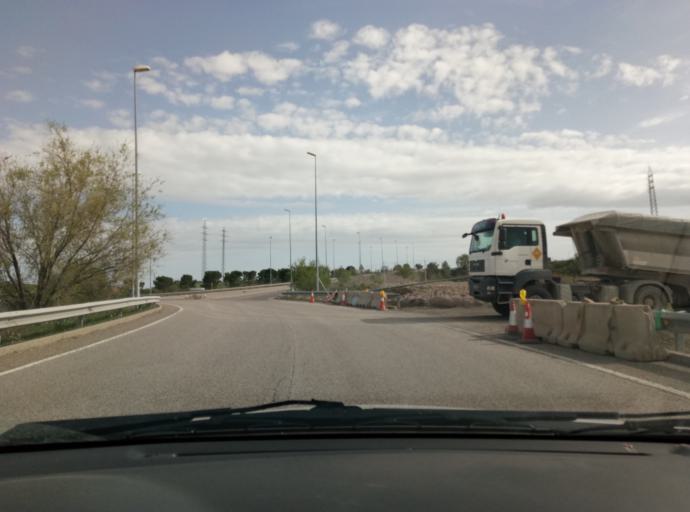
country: ES
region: Catalonia
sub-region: Provincia de Lleida
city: Cervera
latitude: 41.6805
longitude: 1.2840
